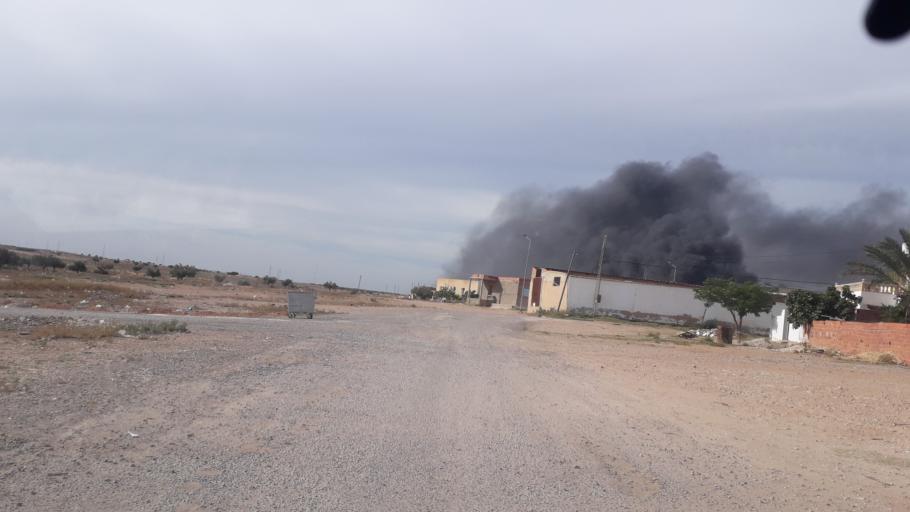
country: TN
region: Safaqis
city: Al Qarmadah
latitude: 34.8868
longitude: 10.7578
